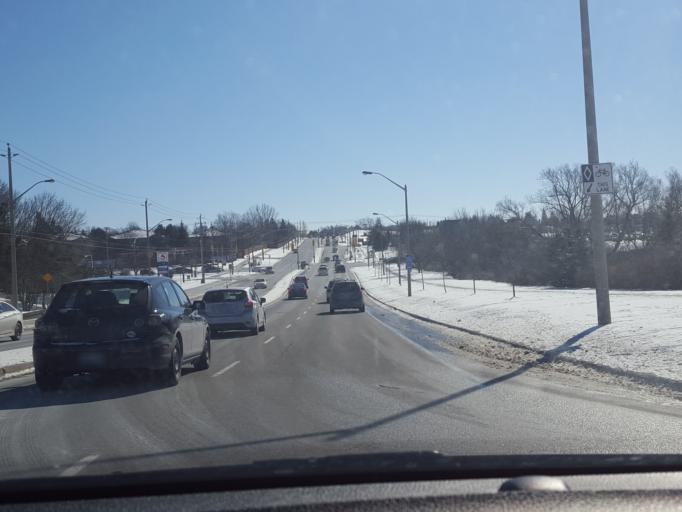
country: CA
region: Ontario
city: Kitchener
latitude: 43.4337
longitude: -80.5269
